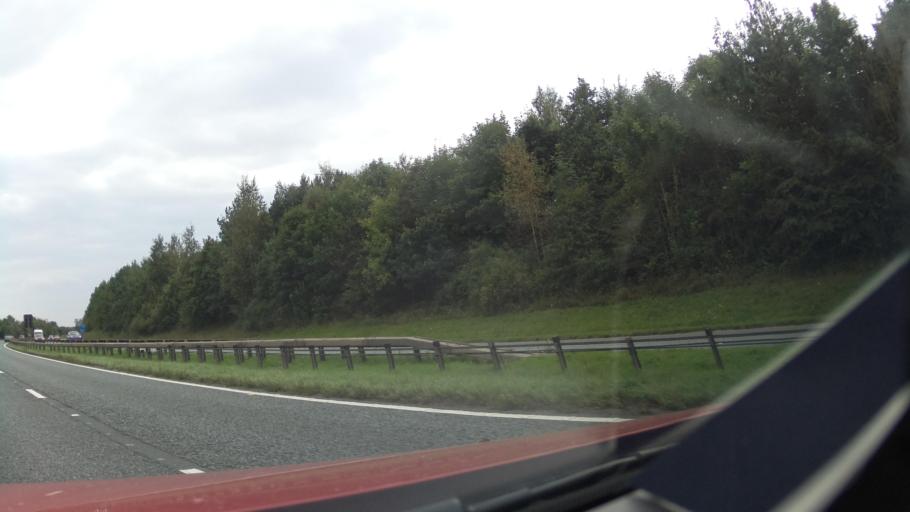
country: GB
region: England
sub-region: County Durham
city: Coxhoe
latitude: 54.7398
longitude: -1.5145
